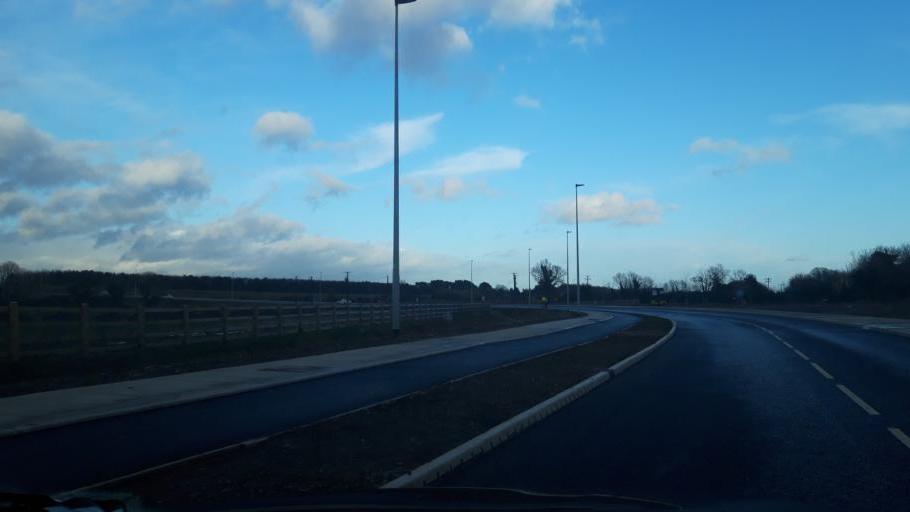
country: IE
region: Leinster
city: Donabate
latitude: 53.4792
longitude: -6.1431
